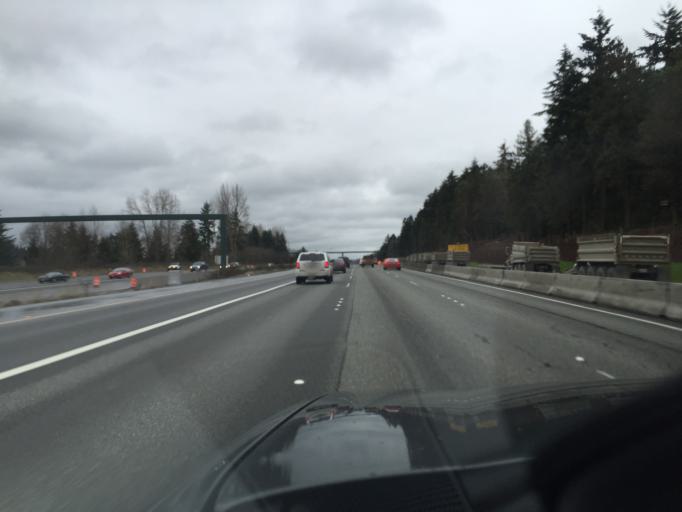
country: US
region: Washington
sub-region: King County
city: Kingsgate
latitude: 47.7276
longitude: -122.1890
